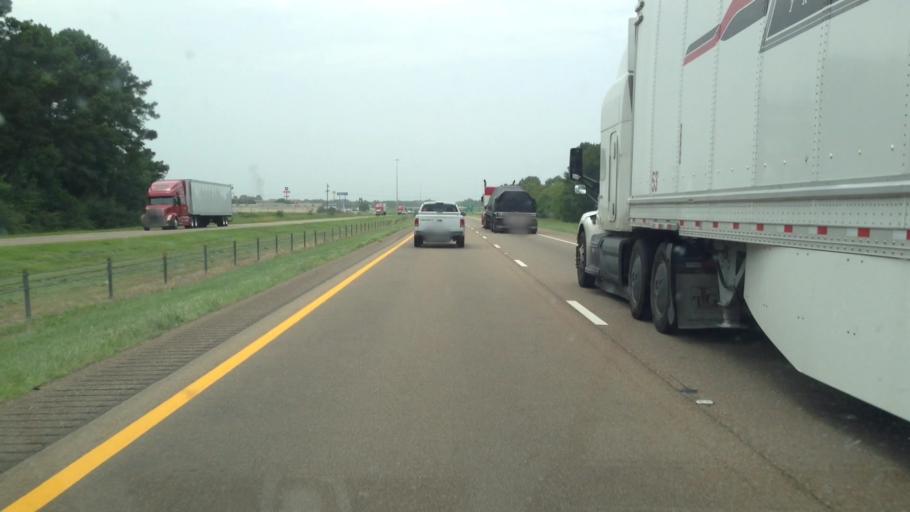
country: US
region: Texas
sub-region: Bowie County
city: New Boston
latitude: 33.4733
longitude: -94.3957
